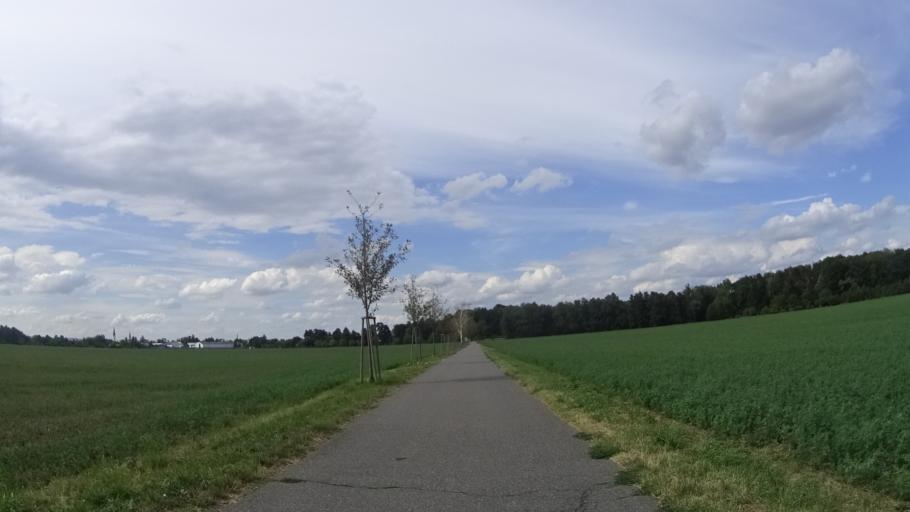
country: CZ
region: Olomoucky
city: Litovel
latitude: 49.6938
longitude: 17.0946
